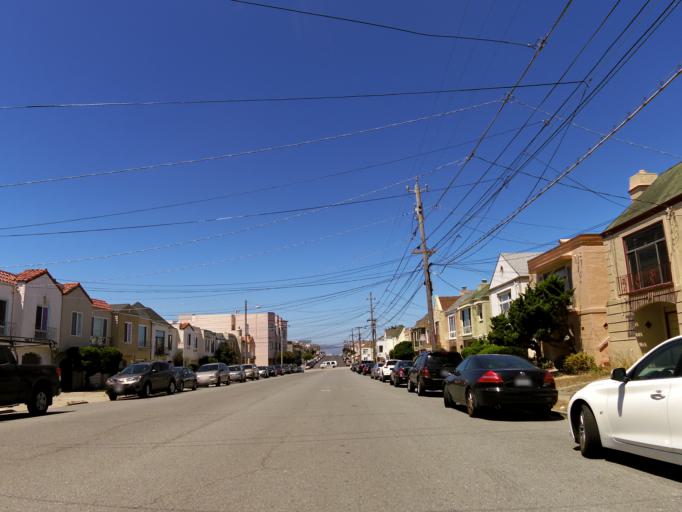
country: US
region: California
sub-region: San Mateo County
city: Daly City
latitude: 37.7525
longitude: -122.4882
